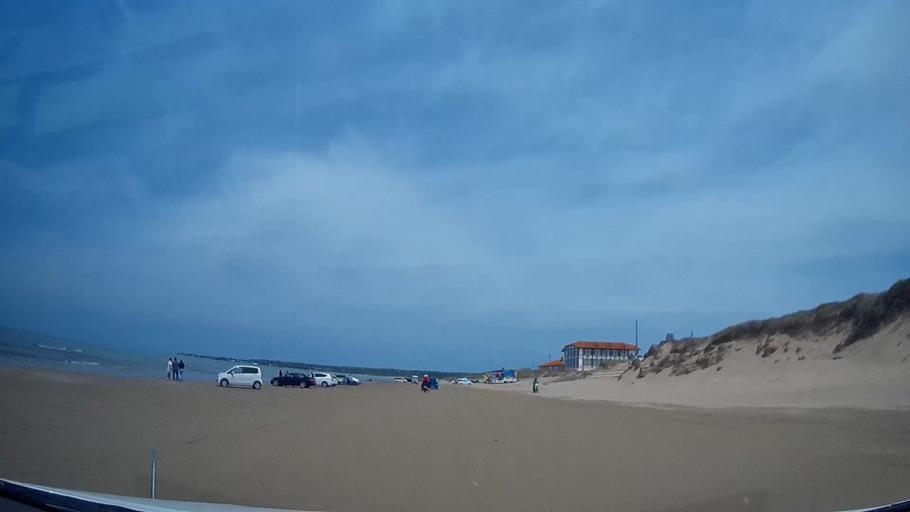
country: JP
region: Ishikawa
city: Hakui
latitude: 36.8915
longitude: 136.7654
